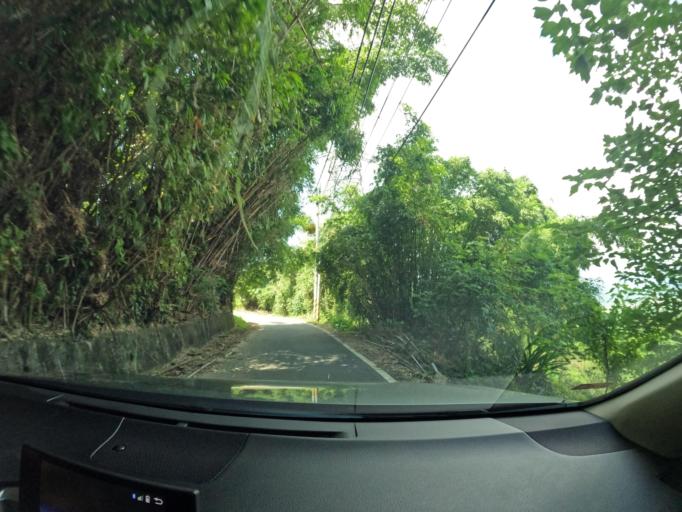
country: TW
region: Taiwan
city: Fengyuan
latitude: 24.3151
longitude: 120.7652
